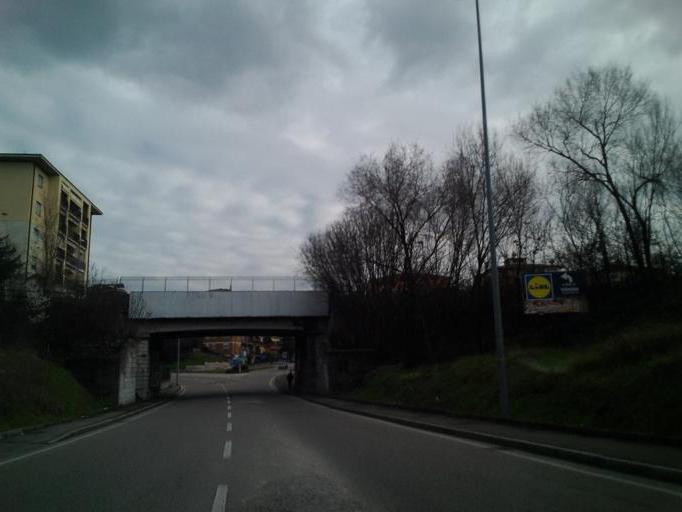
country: IT
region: Veneto
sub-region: Provincia di Verona
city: Verona
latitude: 45.4215
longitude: 10.9607
